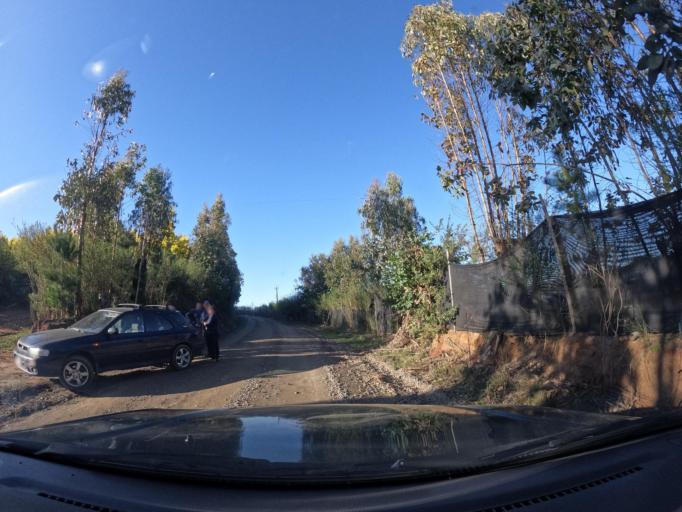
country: CL
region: Biobio
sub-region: Provincia de Concepcion
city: Chiguayante
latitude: -37.0119
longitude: -72.8758
